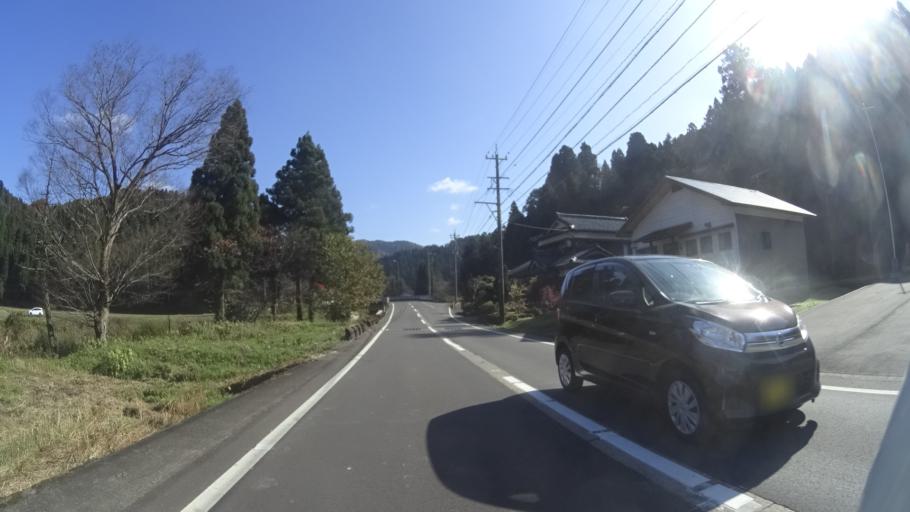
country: JP
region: Fukui
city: Ono
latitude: 35.8780
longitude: 136.3478
